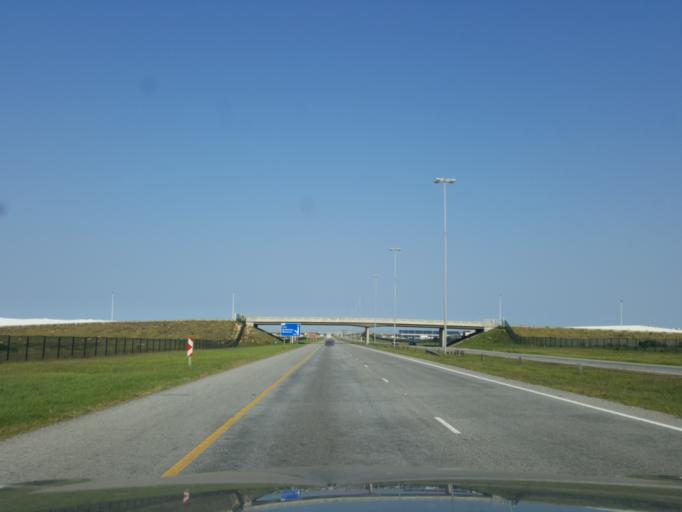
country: ZA
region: Eastern Cape
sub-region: Nelson Mandela Bay Metropolitan Municipality
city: Port Elizabeth
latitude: -33.8107
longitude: 25.6521
